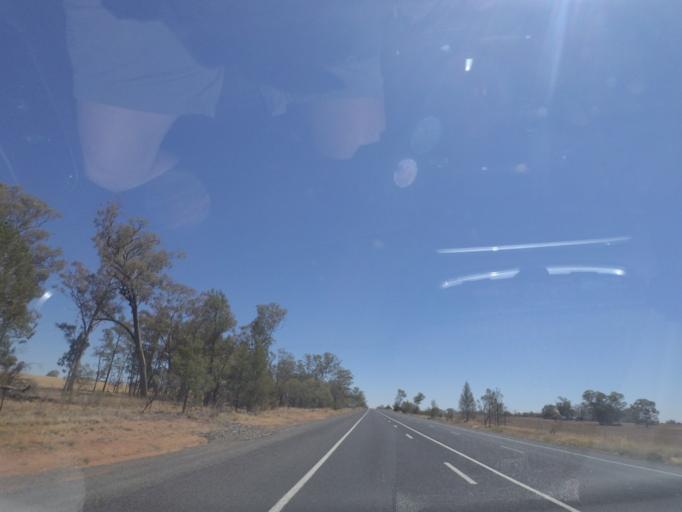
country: AU
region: New South Wales
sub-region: Gilgandra
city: Gilgandra
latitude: -31.4923
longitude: 148.8696
